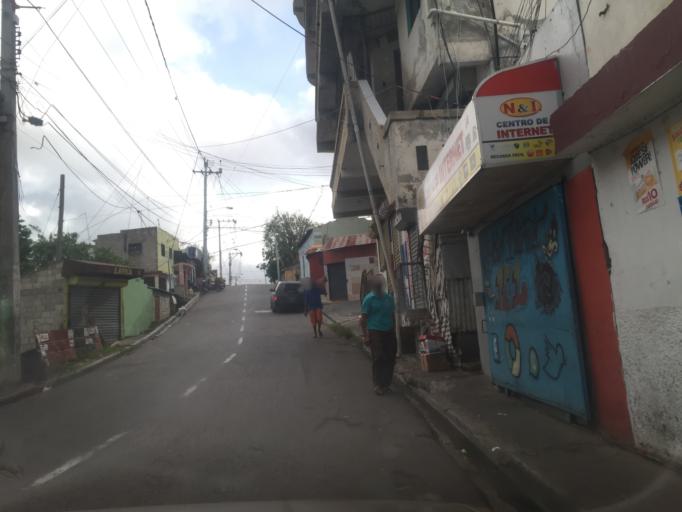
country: DO
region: Santiago
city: Santiago de los Caballeros
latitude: 19.4245
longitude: -70.7169
